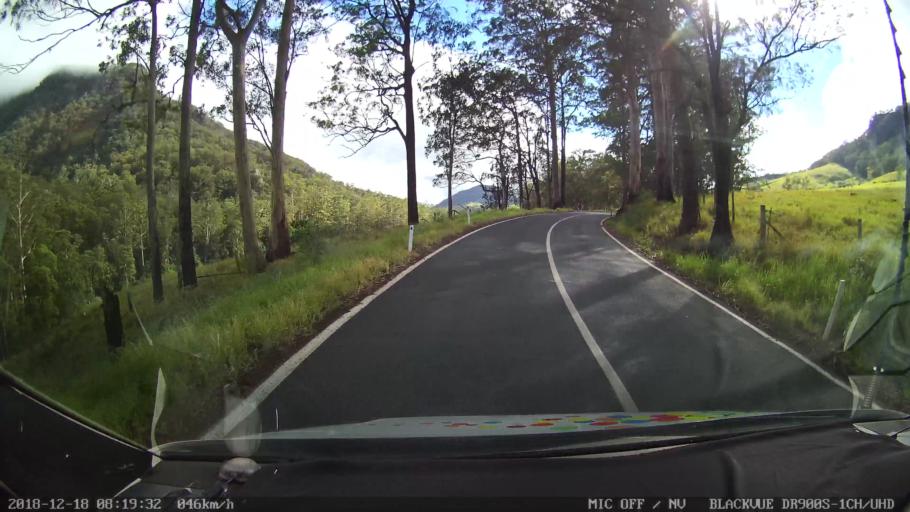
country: AU
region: New South Wales
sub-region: Kyogle
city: Kyogle
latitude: -28.3315
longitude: 152.7095
